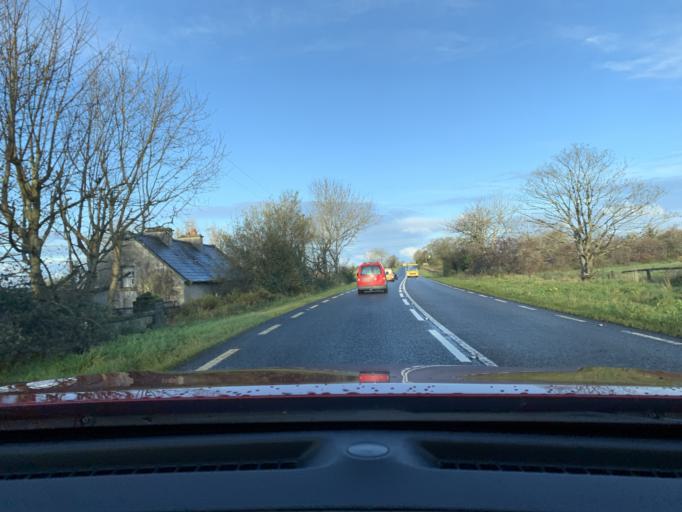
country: IE
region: Connaught
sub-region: Sligo
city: Sligo
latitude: 54.3545
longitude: -8.5139
